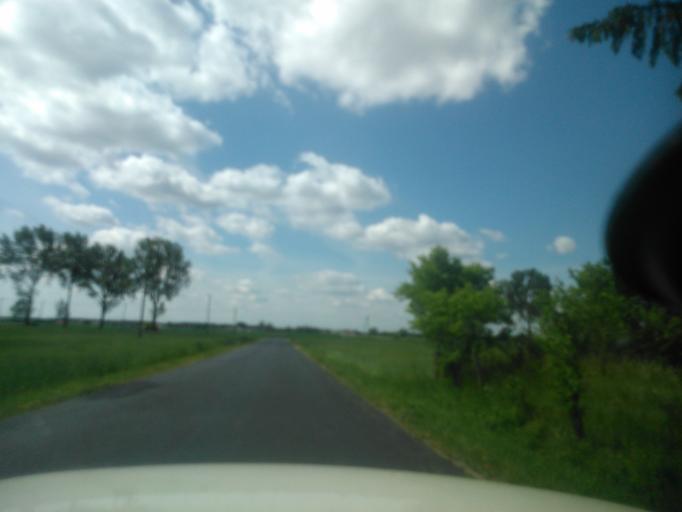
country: PL
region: Kujawsko-Pomorskie
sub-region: Powiat torunski
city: Obrowo
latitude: 53.0049
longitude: 18.8506
